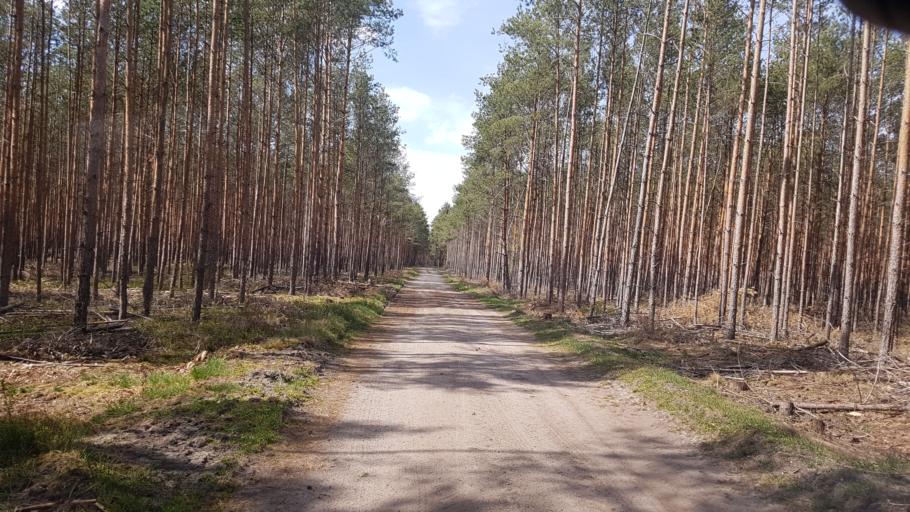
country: DE
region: Brandenburg
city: Ruckersdorf
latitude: 51.5508
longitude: 13.6382
